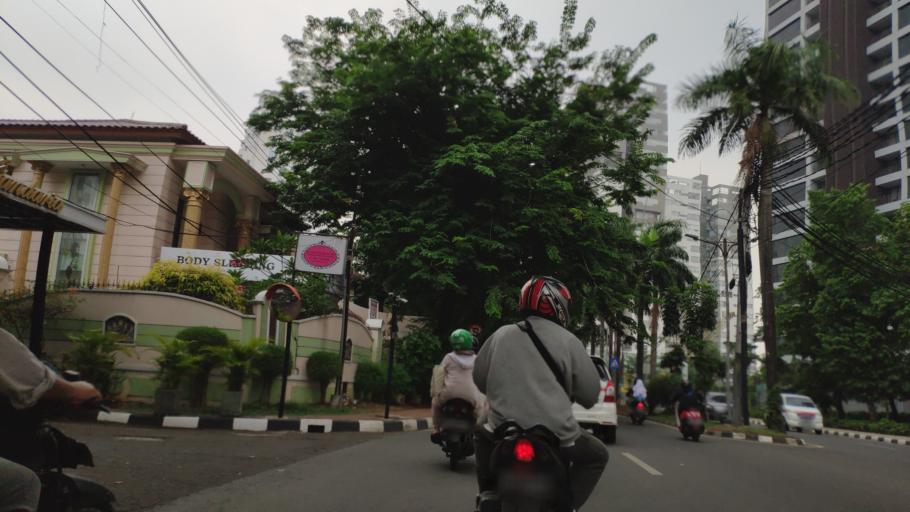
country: ID
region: Jakarta Raya
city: Jakarta
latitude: -6.2457
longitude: 106.7867
